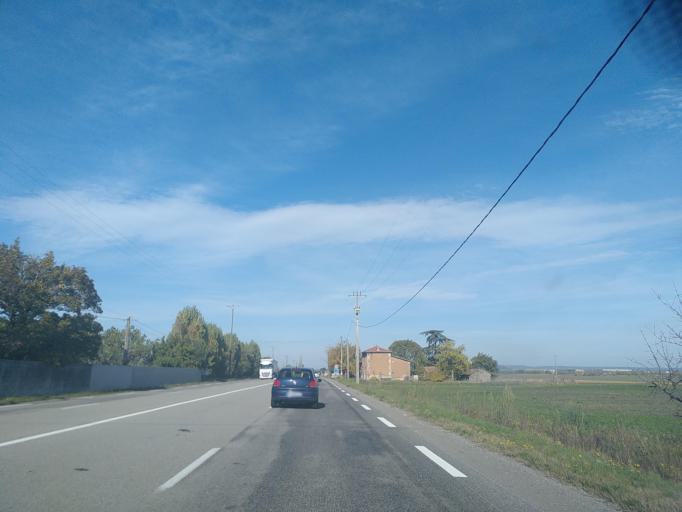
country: FR
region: Rhone-Alpes
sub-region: Departement de la Drome
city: Andancette
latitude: 45.2468
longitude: 4.8211
